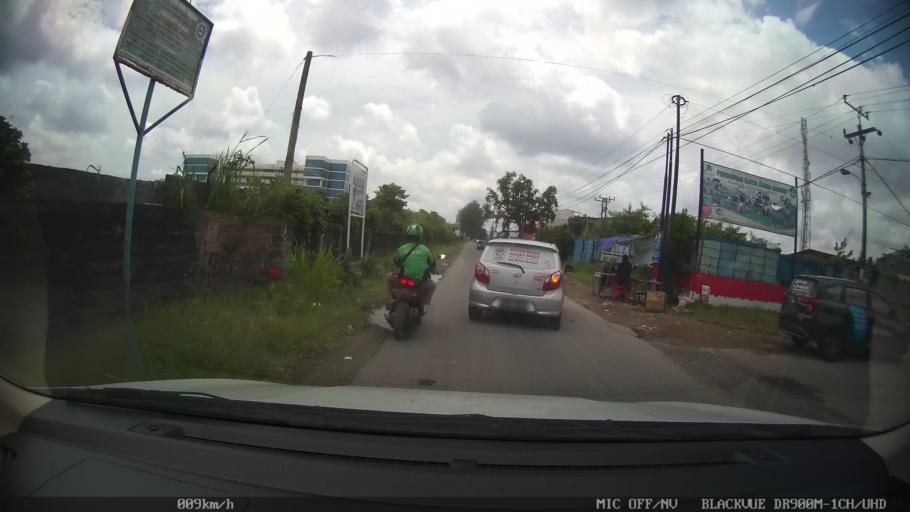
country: ID
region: North Sumatra
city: Medan
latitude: 3.6159
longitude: 98.7293
